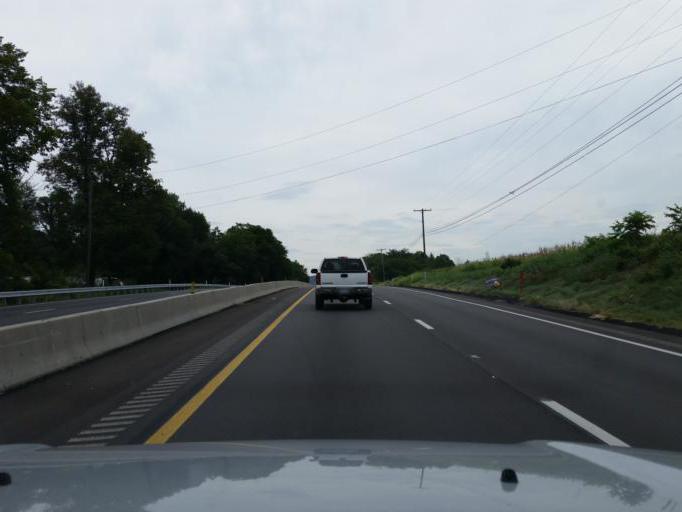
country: US
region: Pennsylvania
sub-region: Westmoreland County
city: Lawson Heights
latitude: 40.2837
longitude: -79.4236
